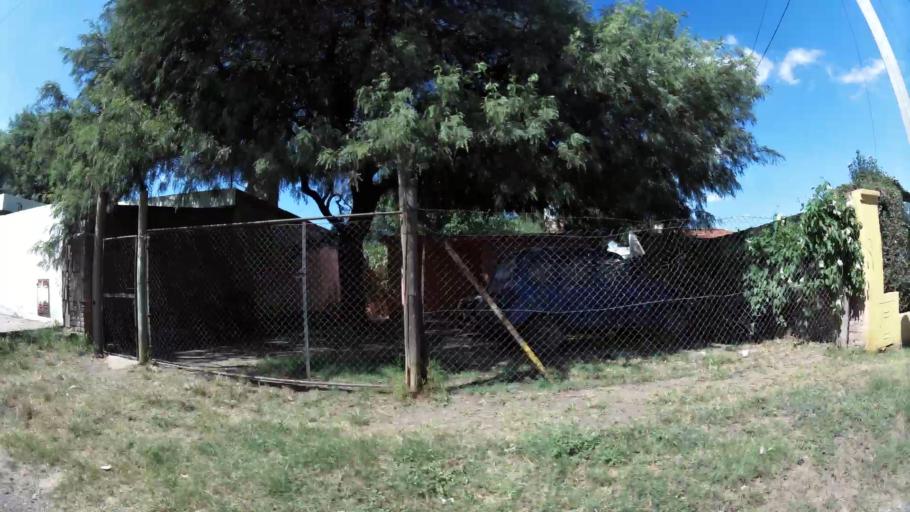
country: AR
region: Cordoba
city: Saldan
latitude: -31.2973
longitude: -64.3046
